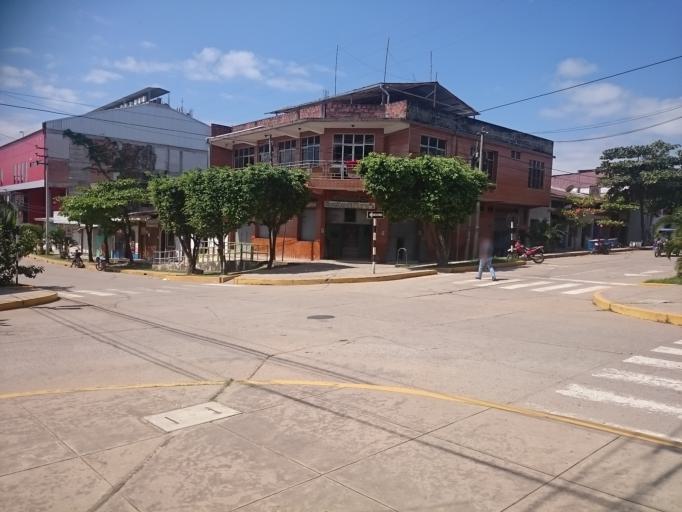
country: PE
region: Ucayali
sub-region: Provincia de Coronel Portillo
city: Pucallpa
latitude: -8.3836
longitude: -74.5293
